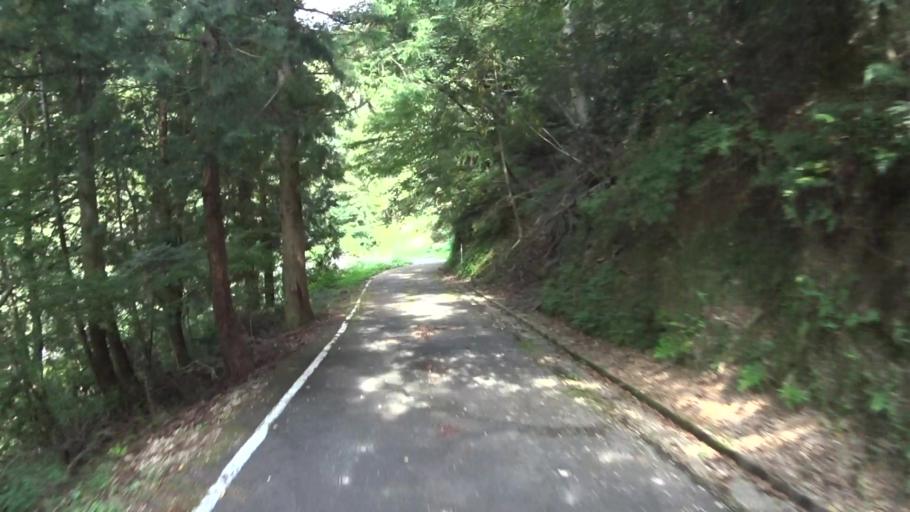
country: JP
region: Kyoto
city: Miyazu
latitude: 35.6655
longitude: 135.1315
